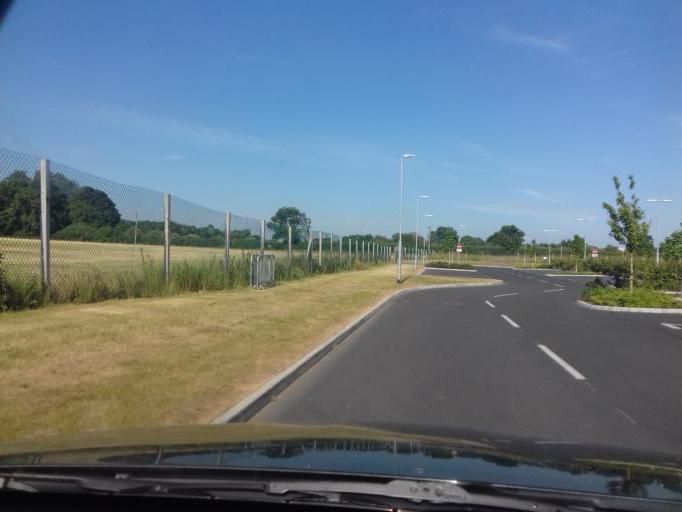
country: IE
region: Leinster
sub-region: Fingal County
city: Blanchardstown
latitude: 53.3996
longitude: -6.3611
